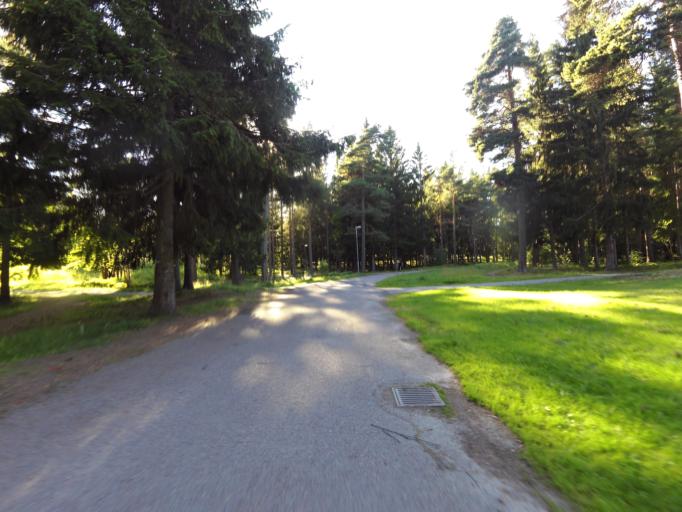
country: SE
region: Gaevleborg
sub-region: Gavle Kommun
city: Gavle
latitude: 60.6525
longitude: 17.1438
